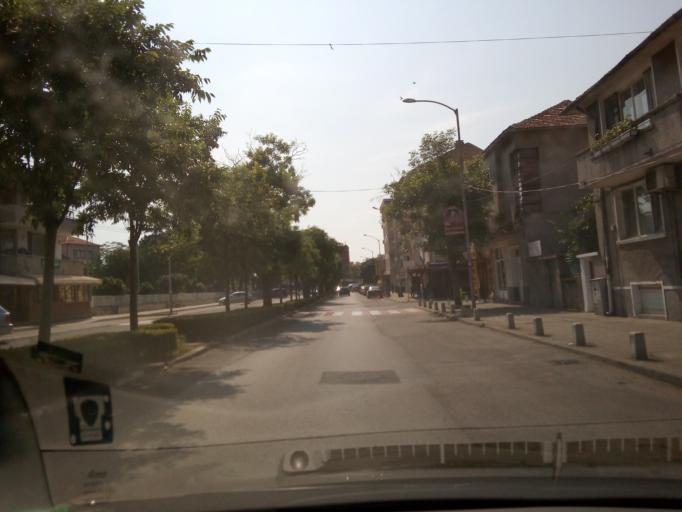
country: BG
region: Burgas
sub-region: Obshtina Pomorie
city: Pomorie
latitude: 42.5603
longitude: 27.6364
